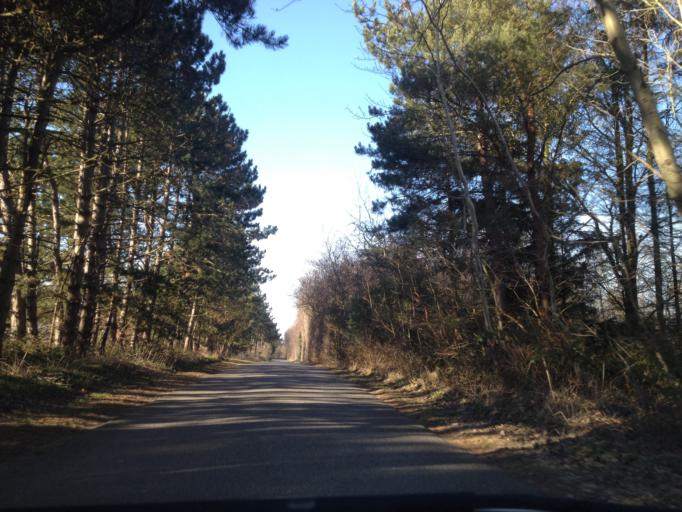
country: DK
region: South Denmark
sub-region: Kerteminde Kommune
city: Kerteminde
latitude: 55.5514
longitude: 10.6216
